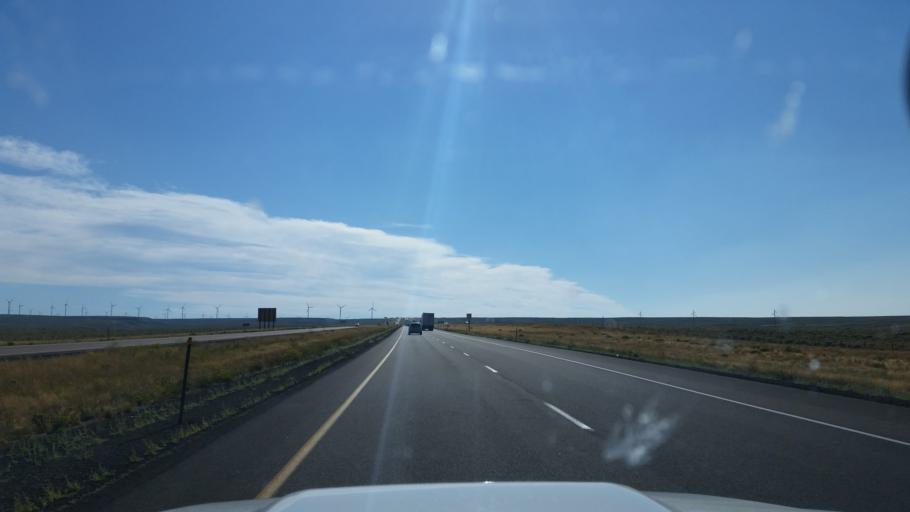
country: US
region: Wyoming
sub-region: Uinta County
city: Mountain View
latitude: 41.3256
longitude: -110.4696
